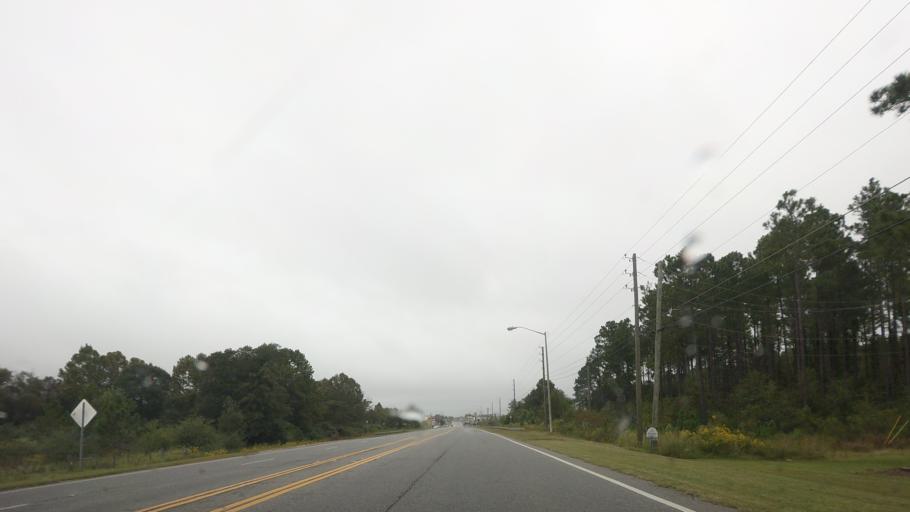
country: US
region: Georgia
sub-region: Ben Hill County
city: Fitzgerald
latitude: 31.6900
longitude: -83.2431
